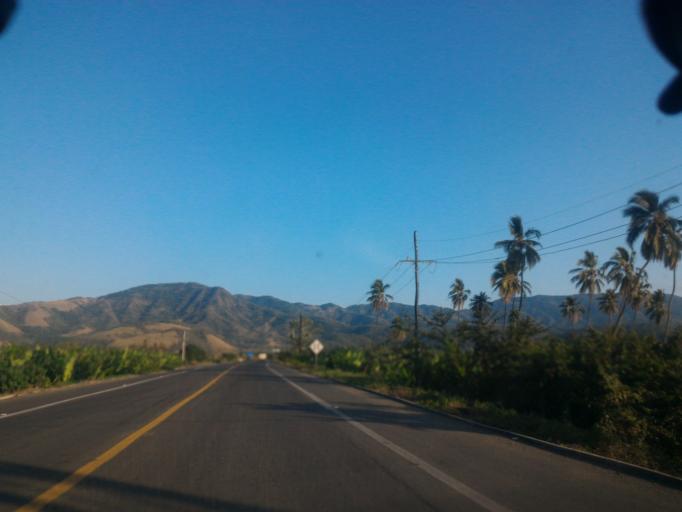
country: MX
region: Michoacan
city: Coahuayana Viejo
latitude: 18.6743
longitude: -103.6787
